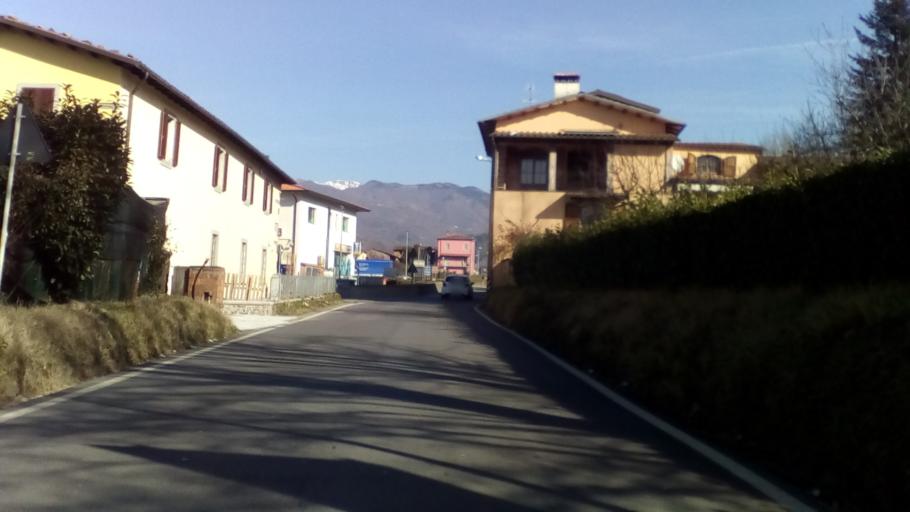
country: IT
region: Tuscany
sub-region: Provincia di Lucca
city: Pieve Fosciana
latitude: 44.1236
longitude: 10.4096
